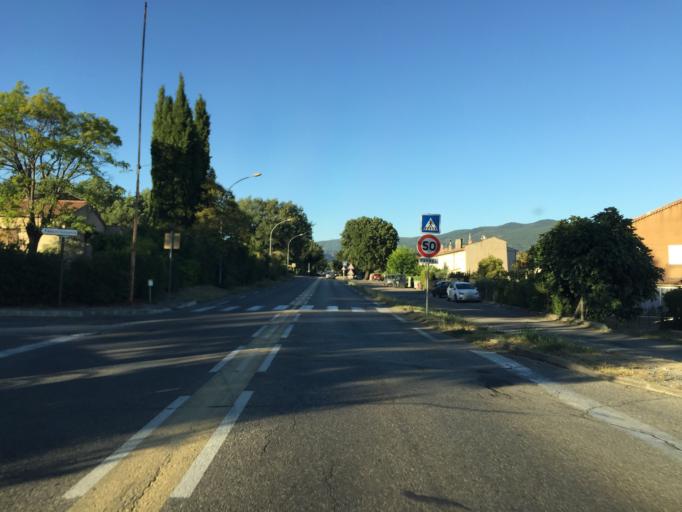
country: FR
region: Provence-Alpes-Cote d'Azur
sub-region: Departement des Alpes-de-Haute-Provence
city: Les Mees
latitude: 44.0713
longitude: 5.9881
